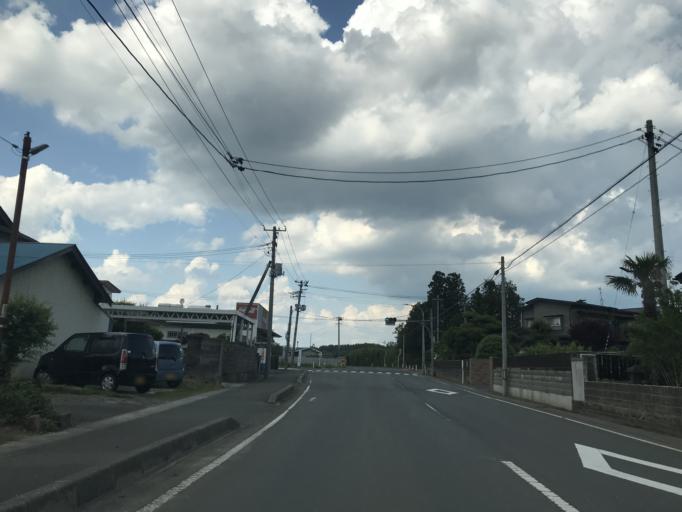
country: JP
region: Miyagi
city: Wakuya
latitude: 38.6300
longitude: 141.2009
